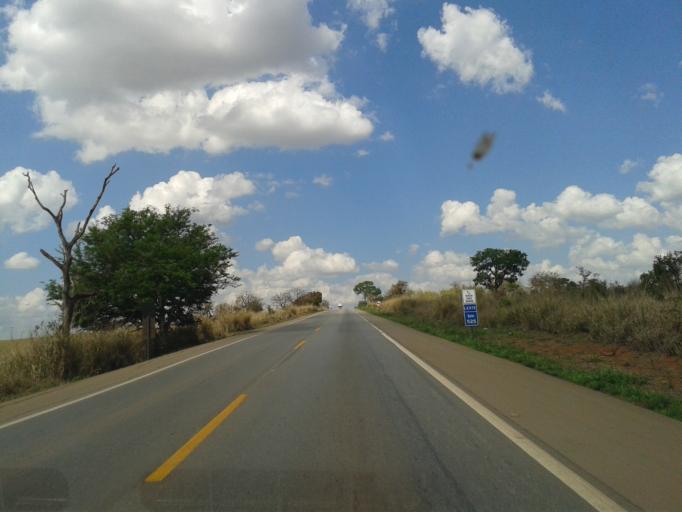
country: BR
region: Minas Gerais
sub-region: Luz
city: Luz
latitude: -19.7840
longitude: -45.7021
